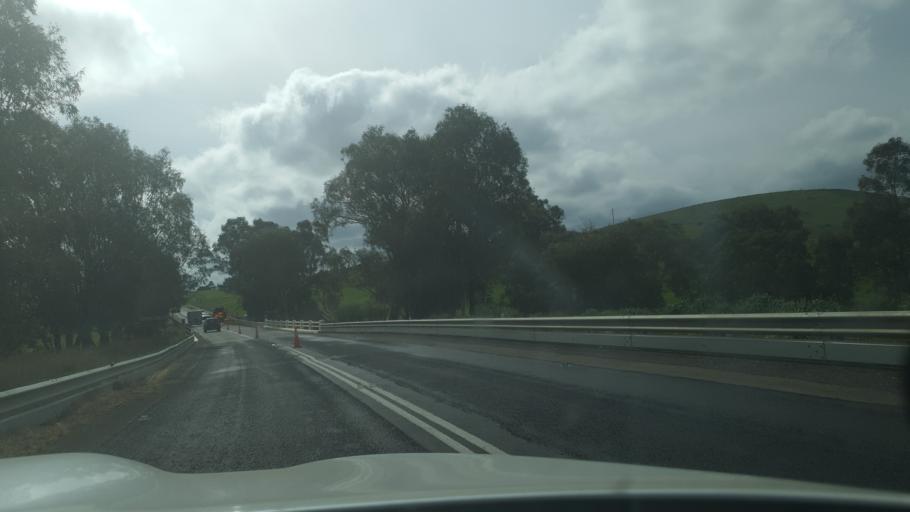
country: AU
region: Victoria
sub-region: Central Goldfields
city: Maryborough
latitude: -37.2143
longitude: 143.7276
